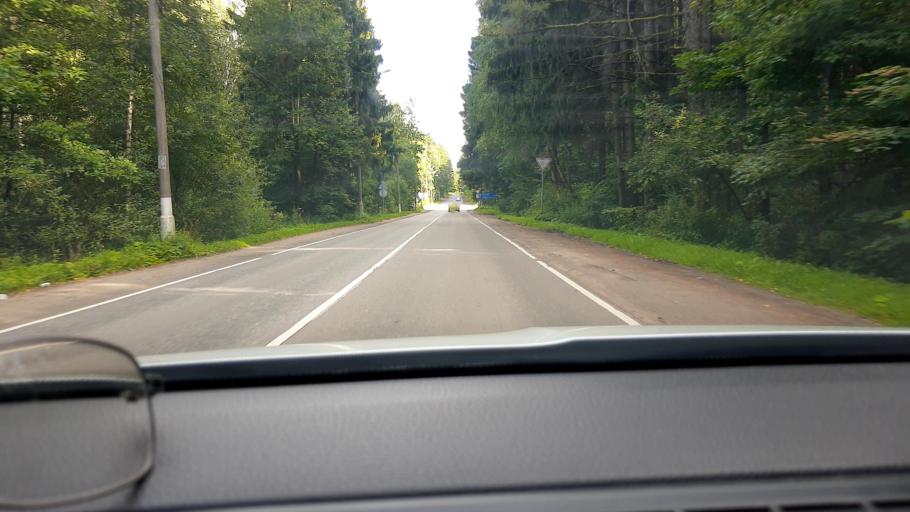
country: RU
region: Moskovskaya
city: Povedniki
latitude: 55.9721
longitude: 37.6099
